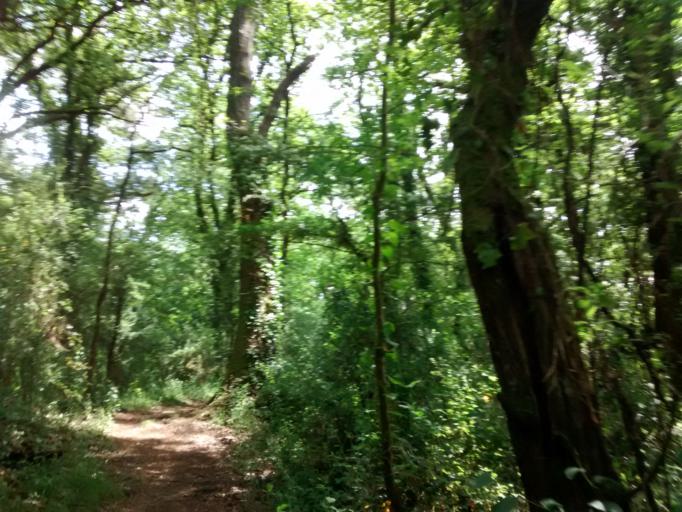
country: FR
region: Brittany
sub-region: Departement du Morbihan
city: Larmor-Baden
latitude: 47.6000
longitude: -2.9004
